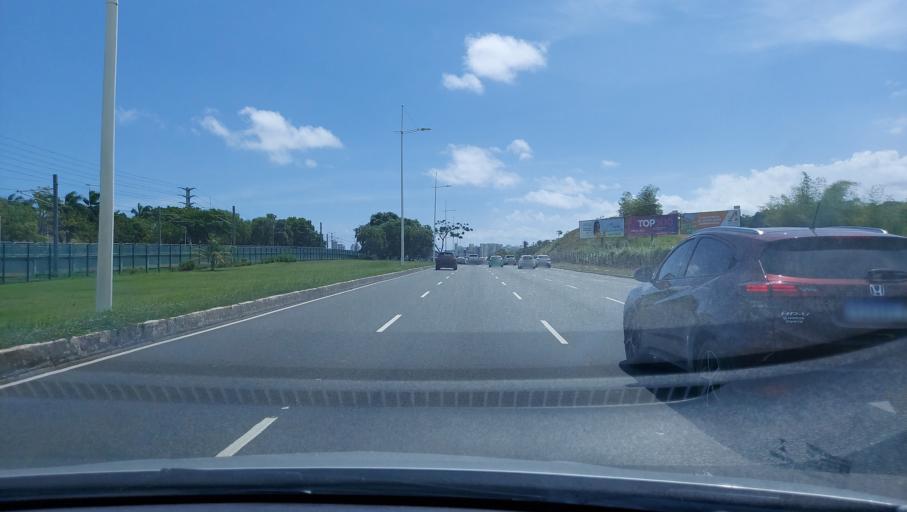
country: BR
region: Bahia
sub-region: Lauro De Freitas
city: Lauro de Freitas
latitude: -12.9303
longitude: -38.3898
